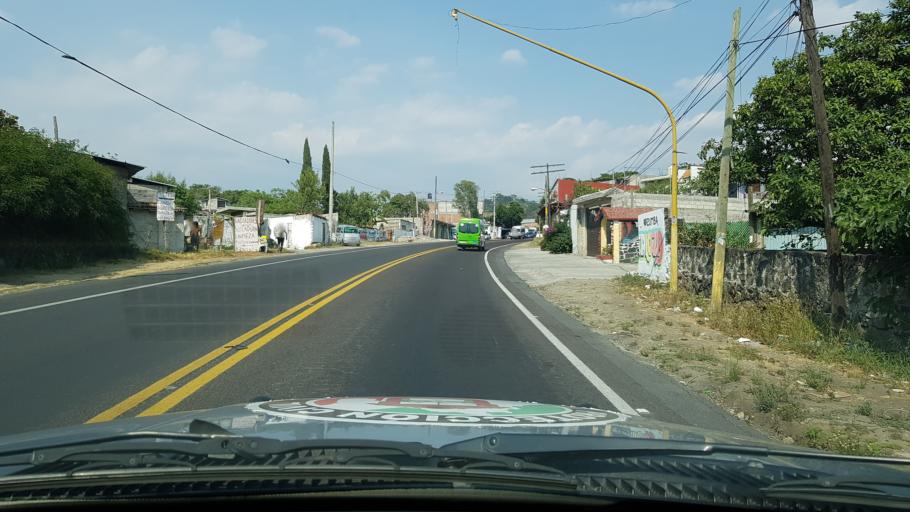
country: MX
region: Mexico
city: Tepetlixpa
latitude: 19.0239
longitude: -98.8227
